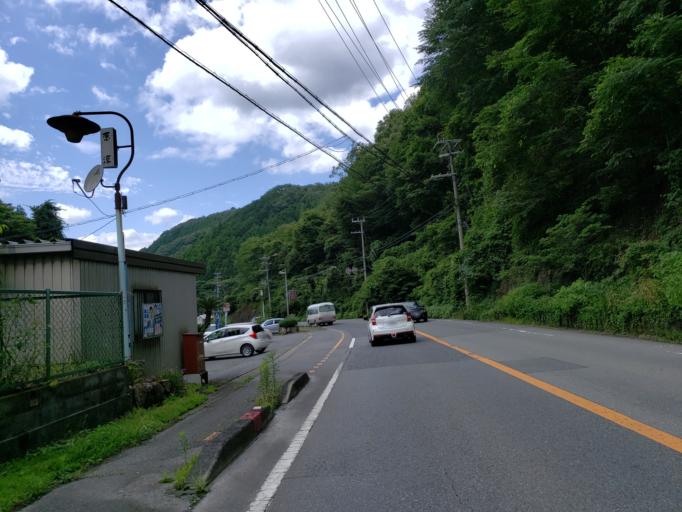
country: JP
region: Hyogo
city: Yamazakicho-nakabirose
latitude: 34.9852
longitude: 134.6108
